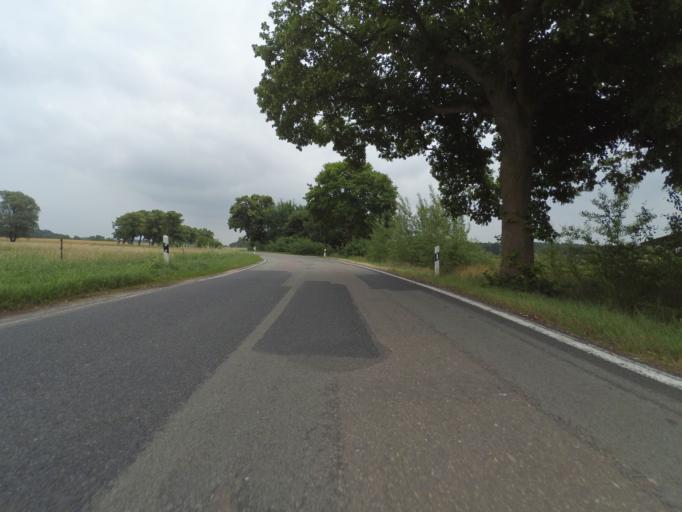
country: DE
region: Mecklenburg-Vorpommern
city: Siggelkow
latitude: 53.3783
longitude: 11.9808
